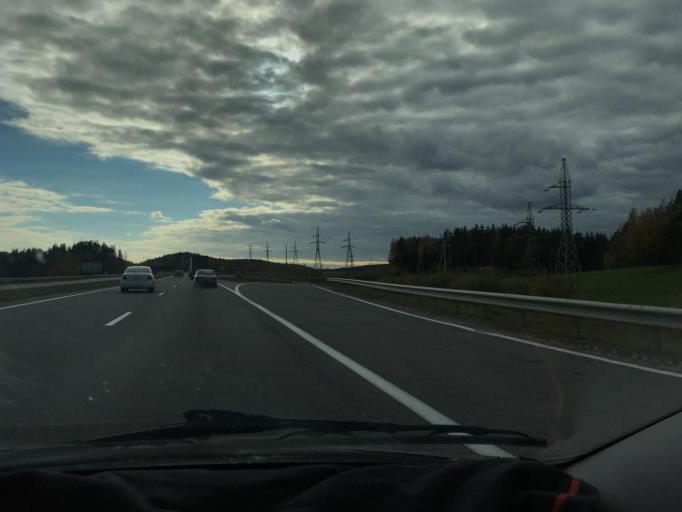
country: BY
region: Minsk
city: Lahoysk
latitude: 54.2099
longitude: 27.8239
